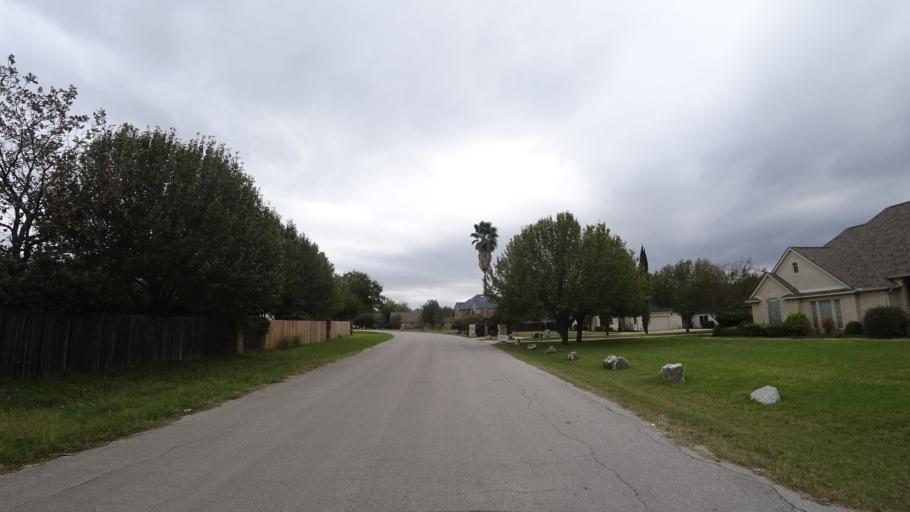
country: US
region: Texas
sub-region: Travis County
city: Shady Hollow
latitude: 30.1508
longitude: -97.8620
